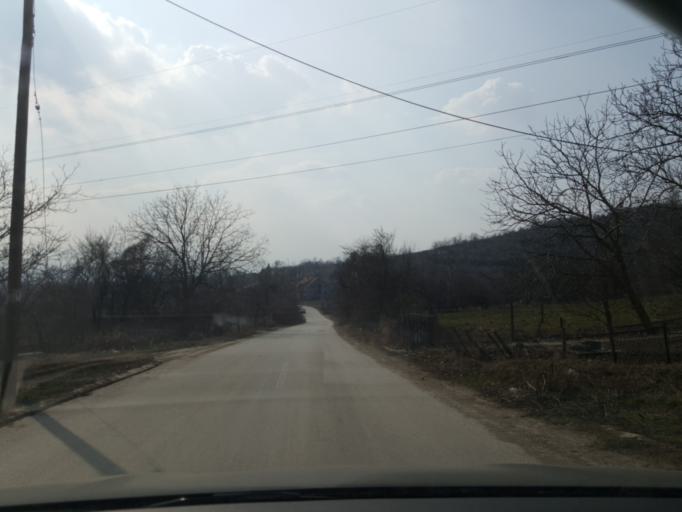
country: RS
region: Central Serbia
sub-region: Nisavski Okrug
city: Aleksinac
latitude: 43.5400
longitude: 21.7319
